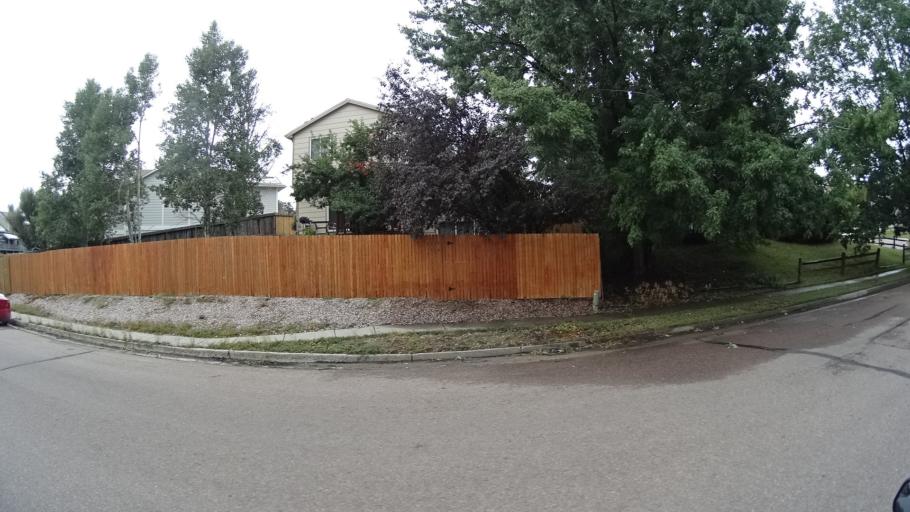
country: US
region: Colorado
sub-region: El Paso County
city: Cimarron Hills
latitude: 38.9194
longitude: -104.7521
